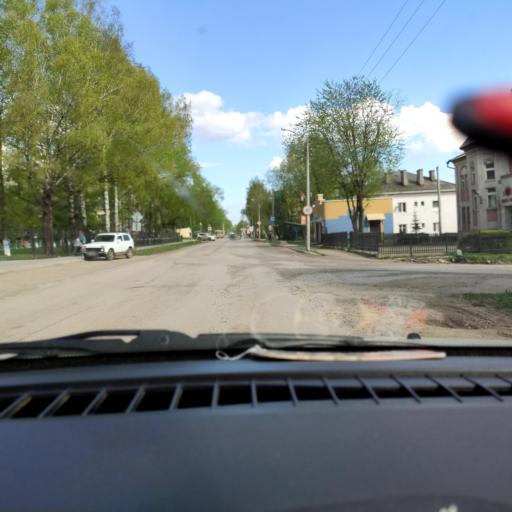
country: RU
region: Perm
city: Kudymkar
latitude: 59.0115
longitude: 54.6545
